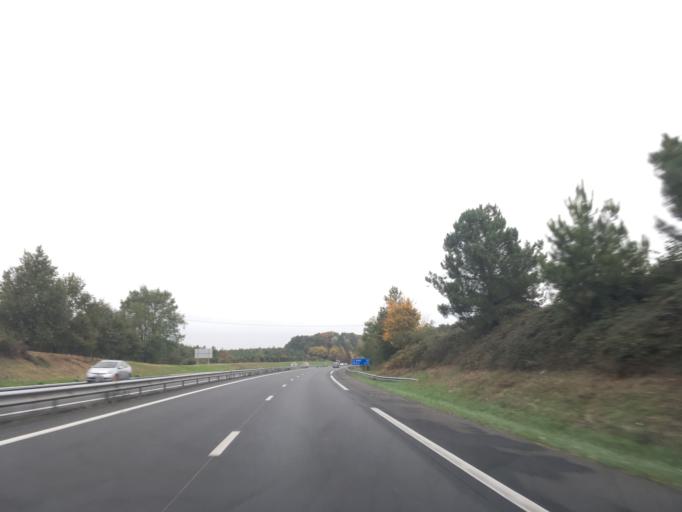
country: FR
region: Pays de la Loire
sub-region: Departement de Maine-et-Loire
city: Seiches-sur-le-Loir
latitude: 47.5720
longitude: -0.3345
